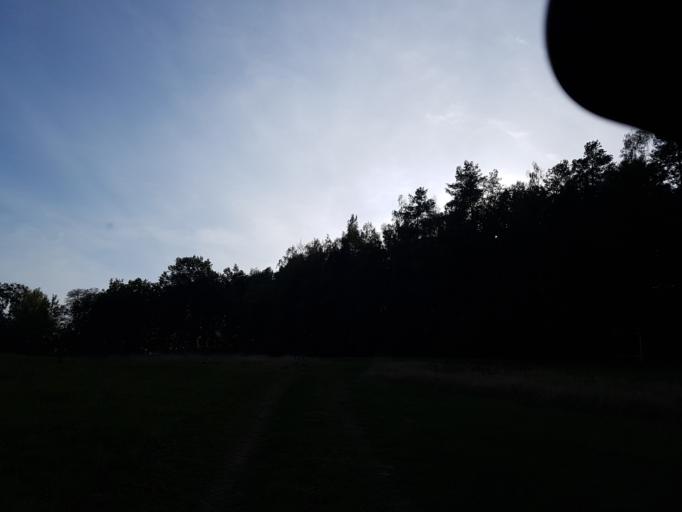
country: DE
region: Saxony
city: Waldheim
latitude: 51.0894
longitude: 13.0246
